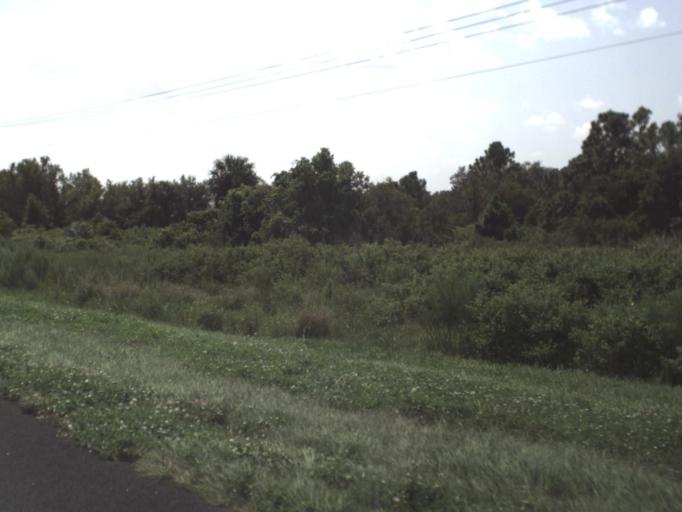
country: US
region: Florida
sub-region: Polk County
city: Frostproof
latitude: 27.6715
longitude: -81.5492
